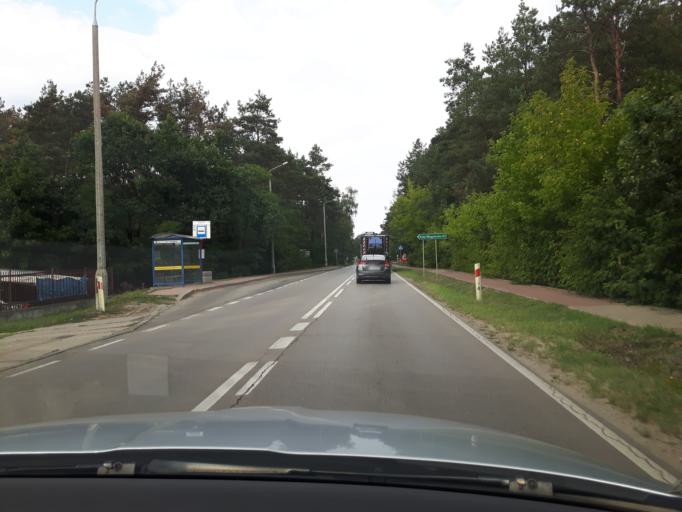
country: PL
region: Masovian Voivodeship
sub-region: Powiat legionowski
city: Stanislawow Pierwszy
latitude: 52.3846
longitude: 21.0298
